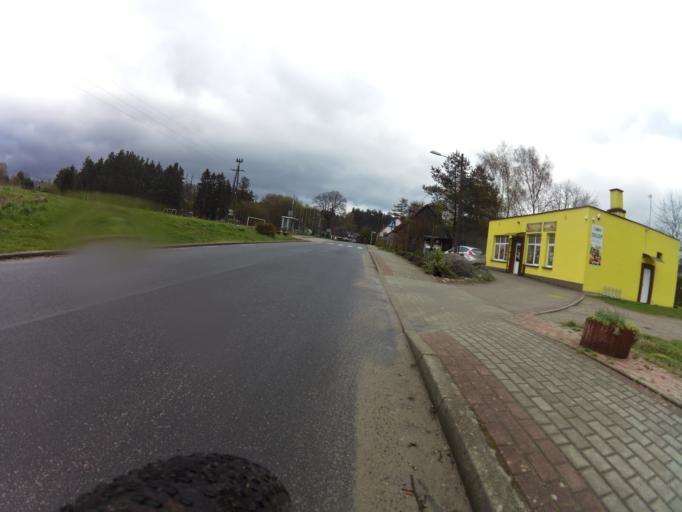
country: PL
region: Pomeranian Voivodeship
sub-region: Powiat slupski
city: Kepice
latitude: 54.2822
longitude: 16.8135
